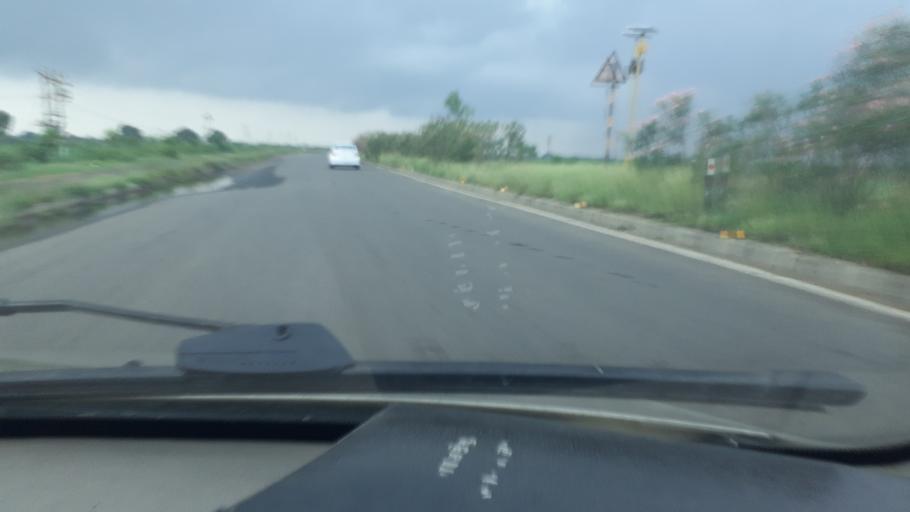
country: IN
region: Tamil Nadu
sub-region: Thoothukkudi
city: Kovilpatti
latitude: 9.1124
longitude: 77.8119
